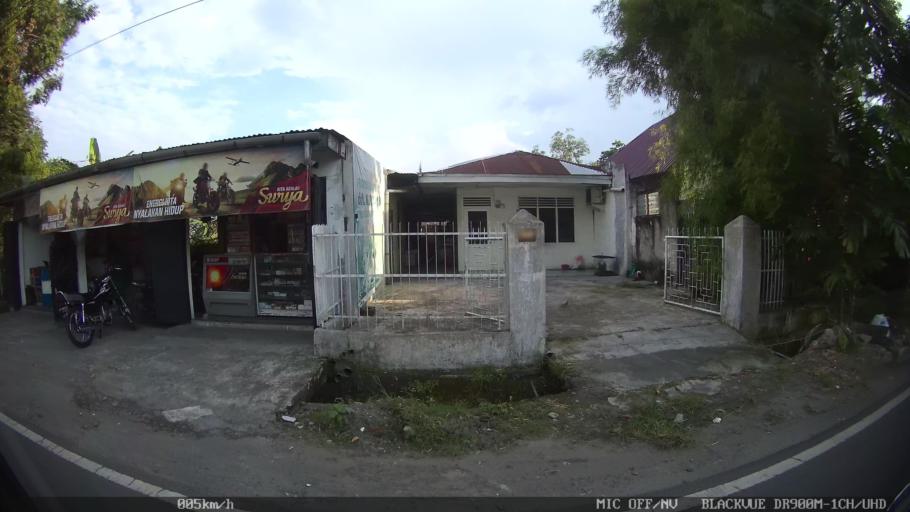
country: ID
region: North Sumatra
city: Medan
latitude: 3.5769
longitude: 98.6518
